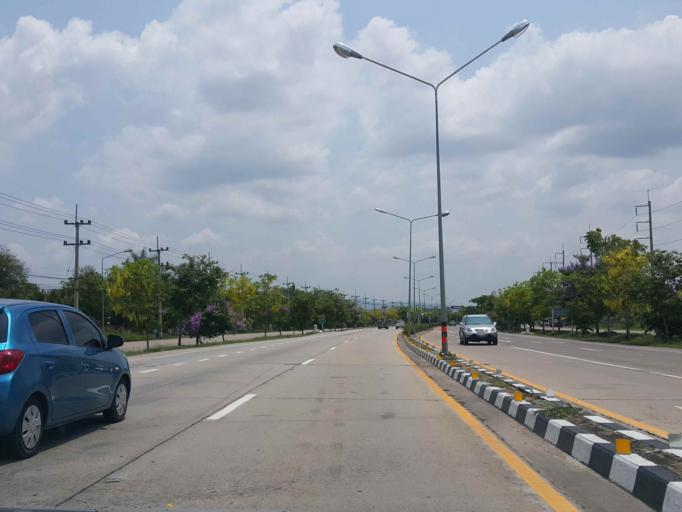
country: TH
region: Lampang
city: Lampang
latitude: 18.2870
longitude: 99.4456
